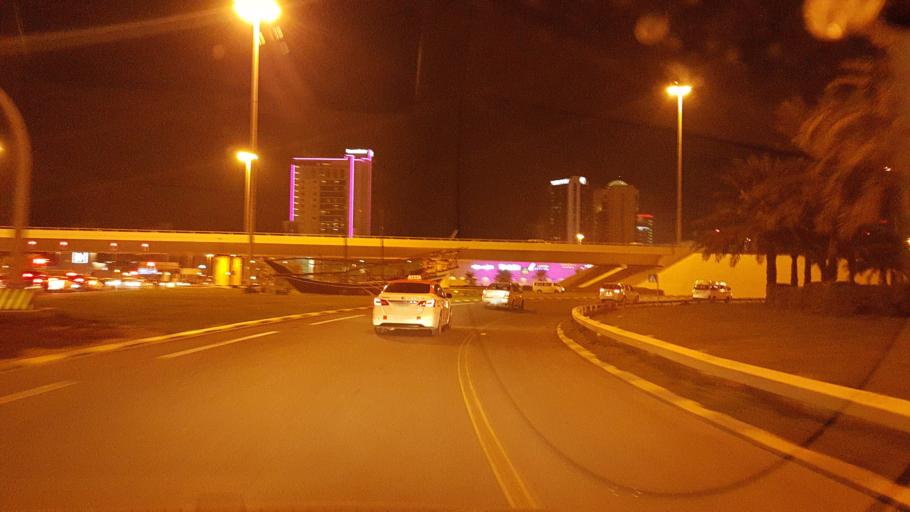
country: BH
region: Manama
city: Jidd Hafs
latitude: 26.2293
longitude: 50.5354
